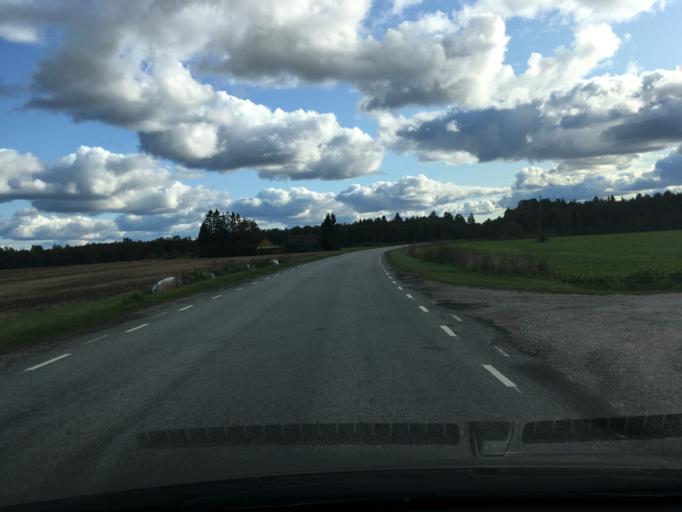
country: EE
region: Harju
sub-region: Raasiku vald
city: Raasiku
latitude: 59.3272
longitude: 25.1599
